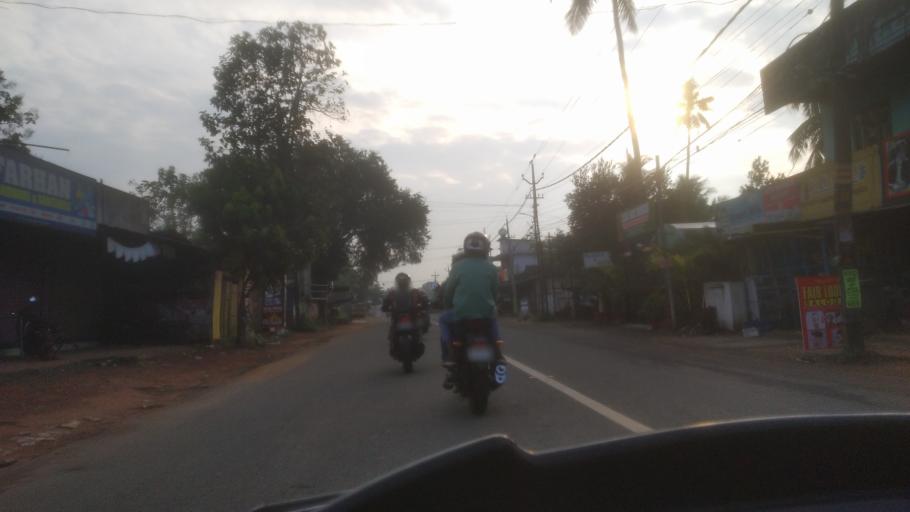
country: IN
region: Kerala
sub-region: Ernakulam
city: Perumpavur
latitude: 10.1159
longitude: 76.4490
